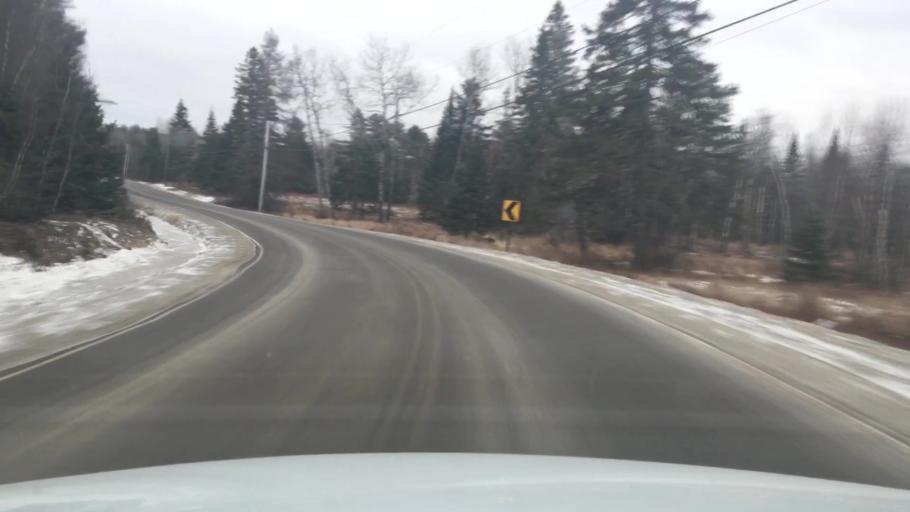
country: US
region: Maine
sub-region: Hancock County
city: Hancock
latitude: 44.5352
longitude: -68.3299
